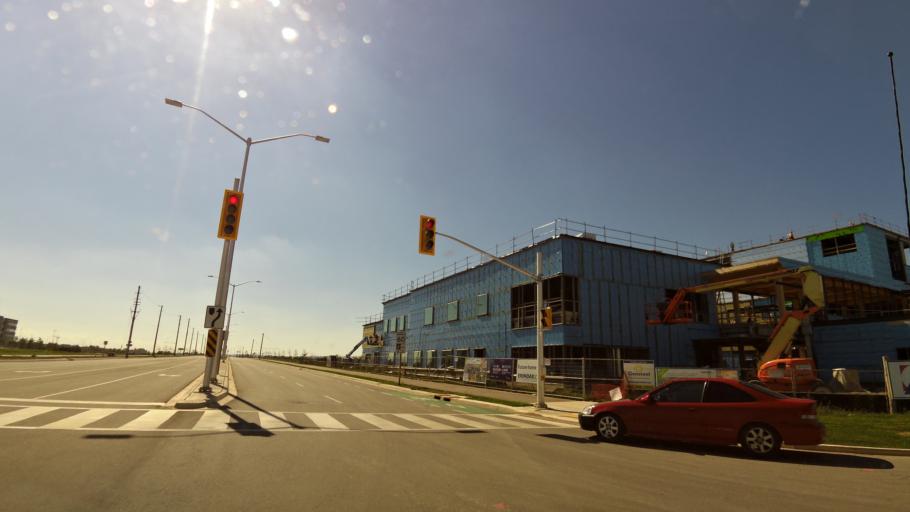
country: CA
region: Ontario
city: Oakville
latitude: 43.4534
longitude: -79.7652
